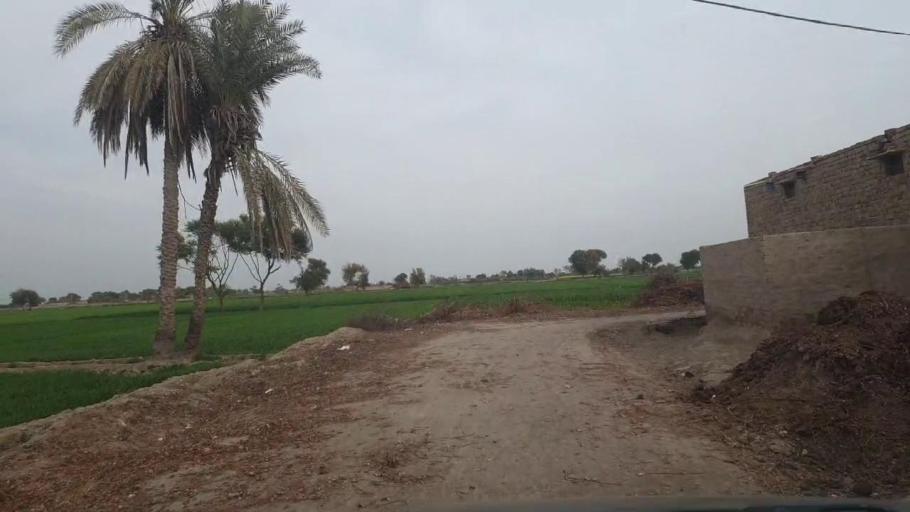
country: PK
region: Sindh
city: Shahpur Chakar
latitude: 26.1150
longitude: 68.5254
